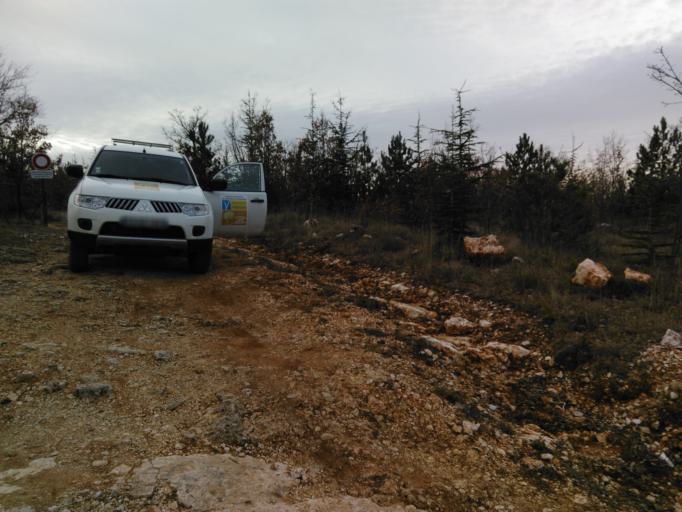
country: FR
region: Provence-Alpes-Cote d'Azur
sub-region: Departement du Vaucluse
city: Villes-sur-Auzon
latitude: 44.0819
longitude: 5.2959
